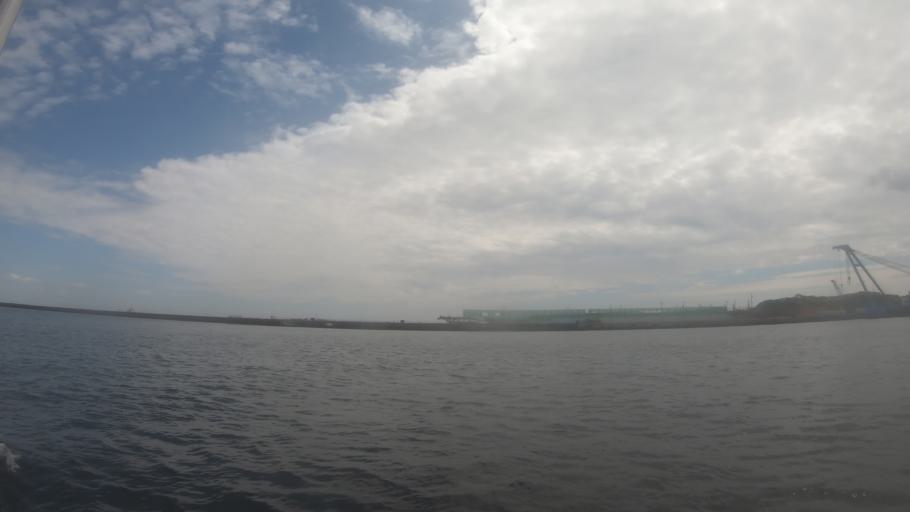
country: JP
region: Kanagawa
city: Yokohama
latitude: 35.3764
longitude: 139.6521
